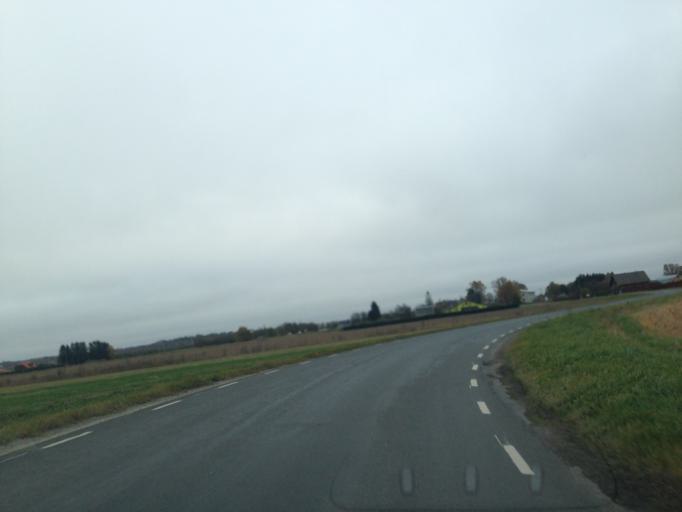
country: EE
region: Harju
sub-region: Saue linn
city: Saue
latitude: 59.3471
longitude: 24.5583
